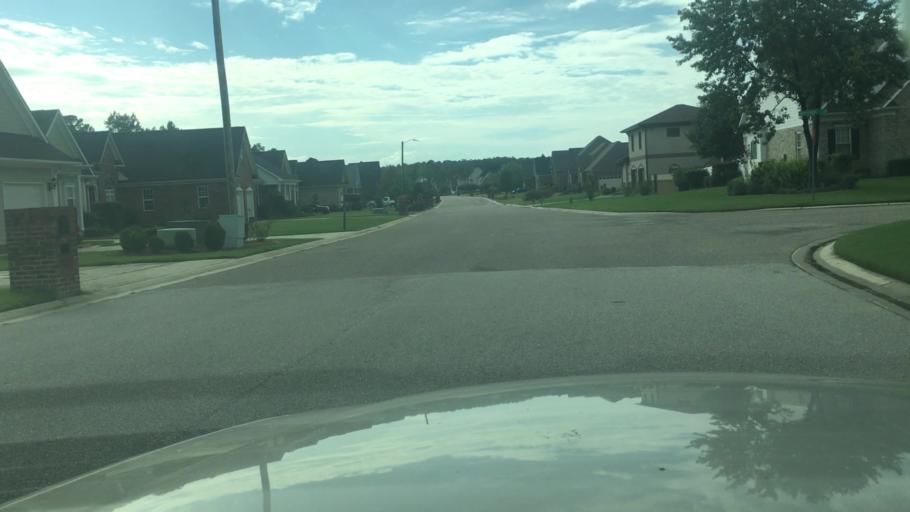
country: US
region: North Carolina
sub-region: Cumberland County
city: Eastover
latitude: 35.1630
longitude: -78.8714
